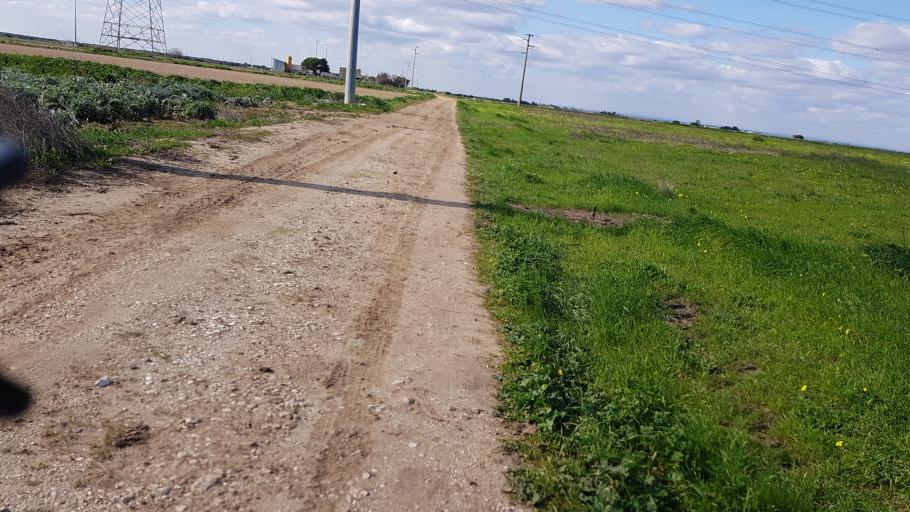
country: IT
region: Apulia
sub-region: Provincia di Brindisi
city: Tuturano
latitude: 40.5751
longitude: 17.9098
